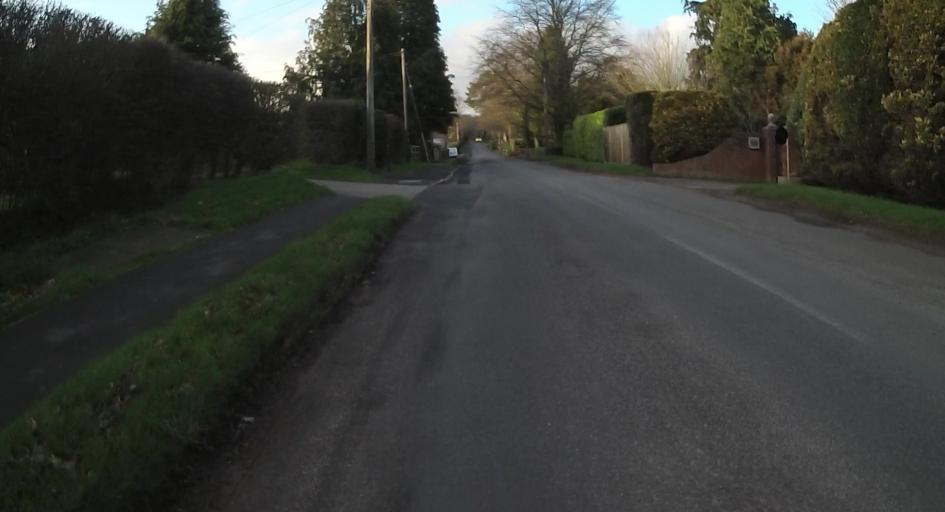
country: GB
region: England
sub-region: Hampshire
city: Four Marks
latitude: 51.1135
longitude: -1.0550
